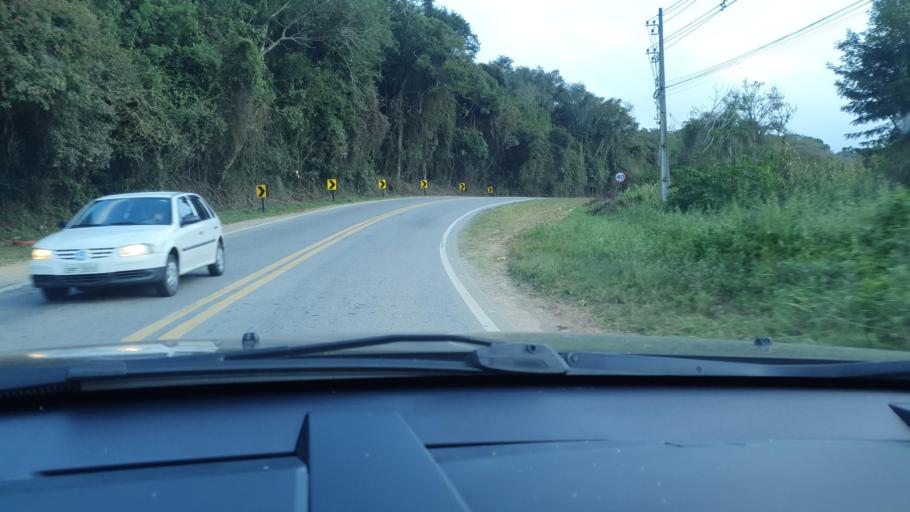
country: BR
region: Sao Paulo
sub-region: Ibiuna
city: Ibiuna
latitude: -23.6825
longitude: -47.2805
